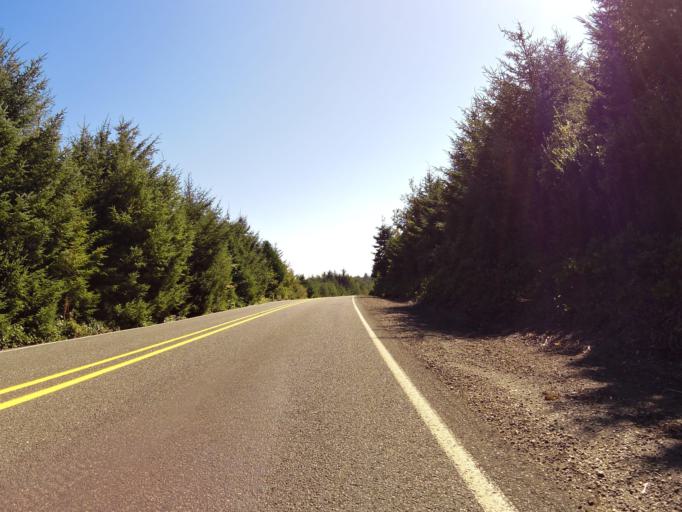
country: US
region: Oregon
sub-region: Coos County
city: Barview
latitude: 43.2704
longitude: -124.3477
